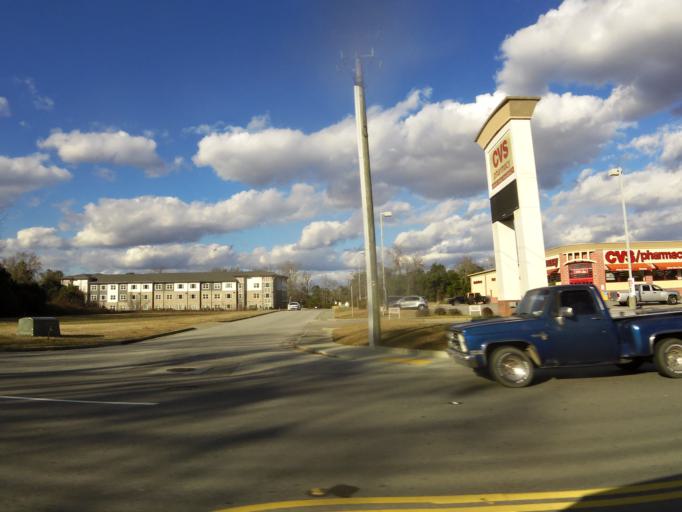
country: US
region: South Carolina
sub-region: Clarendon County
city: Manning
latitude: 33.6954
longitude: -80.2164
